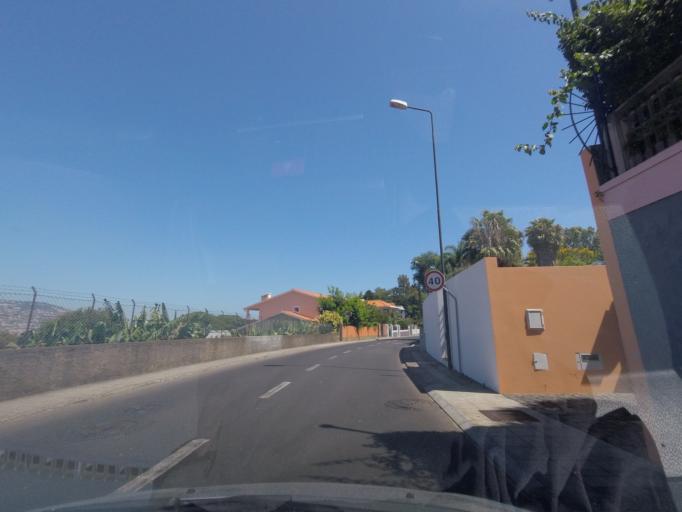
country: PT
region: Madeira
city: Camara de Lobos
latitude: 32.6538
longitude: -16.9357
